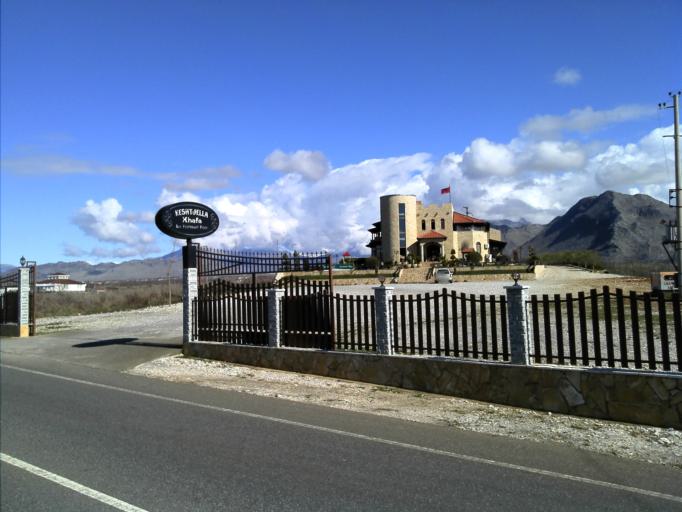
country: AL
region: Shkoder
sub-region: Rrethi i Malesia e Madhe
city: Koplik
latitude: 42.1901
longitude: 19.4561
